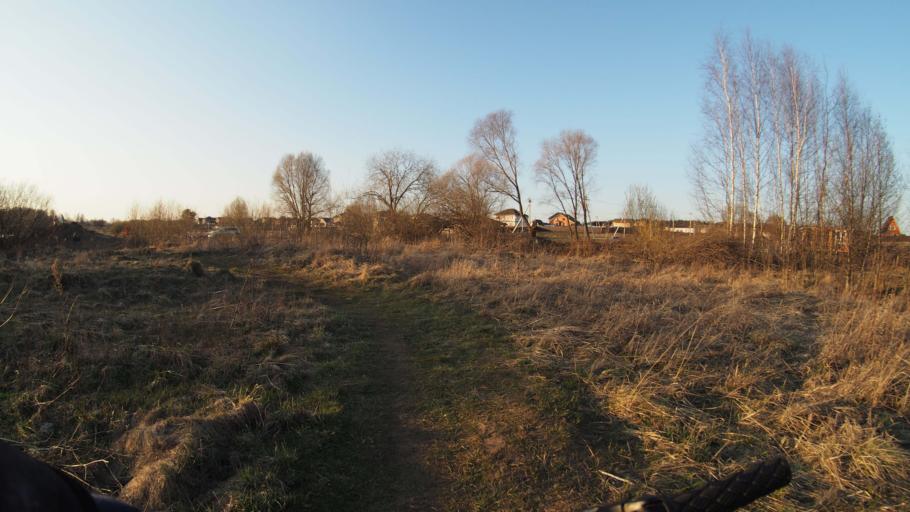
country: RU
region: Moskovskaya
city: Ramenskoye
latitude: 55.5581
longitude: 38.2963
